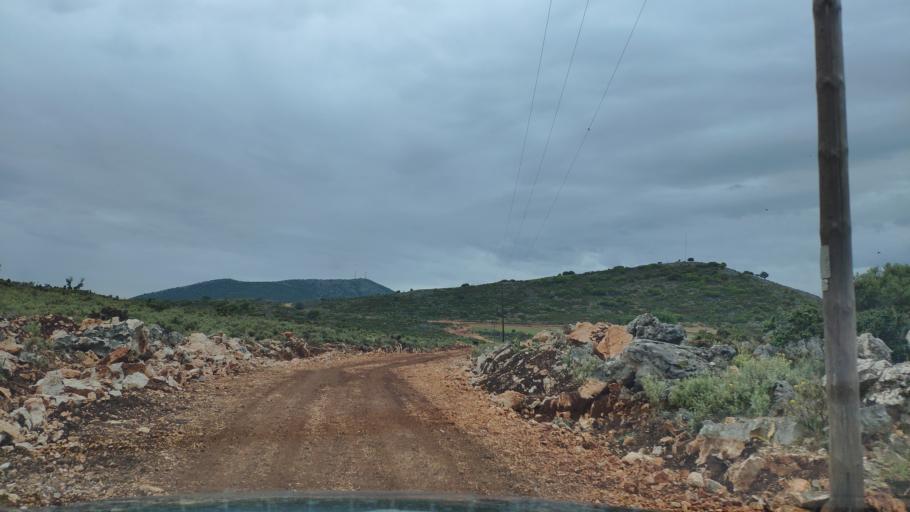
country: GR
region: West Greece
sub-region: Nomos Aitolias kai Akarnanias
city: Archontochorion
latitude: 38.6846
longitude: 21.0287
